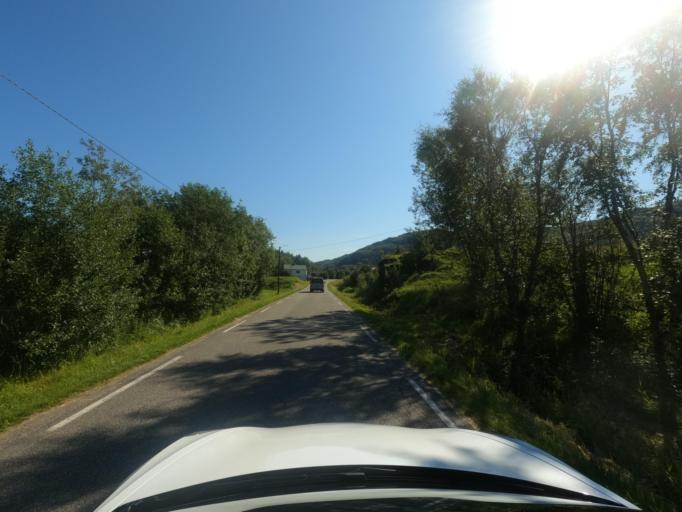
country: NO
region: Nordland
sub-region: Hadsel
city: Stokmarknes
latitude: 68.3026
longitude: 15.0174
